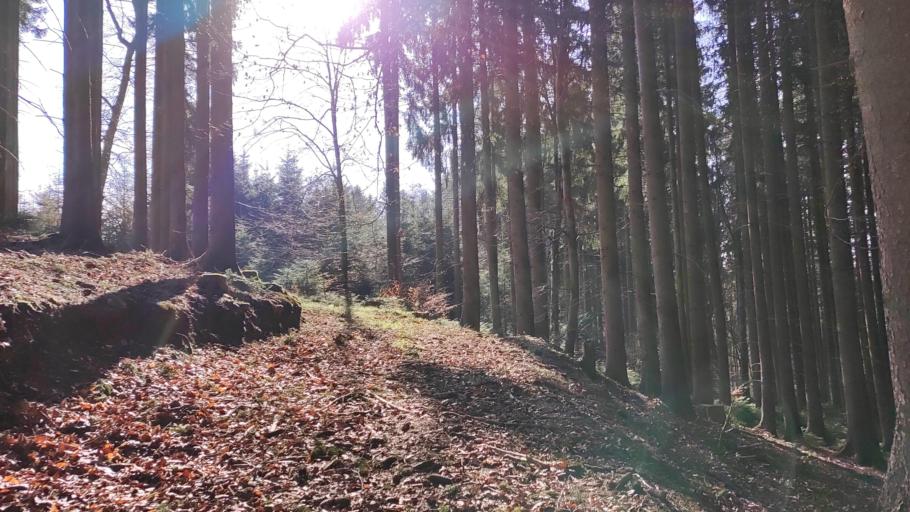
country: DE
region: Bavaria
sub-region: Swabia
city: Zusmarshausen
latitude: 48.4317
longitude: 10.6160
